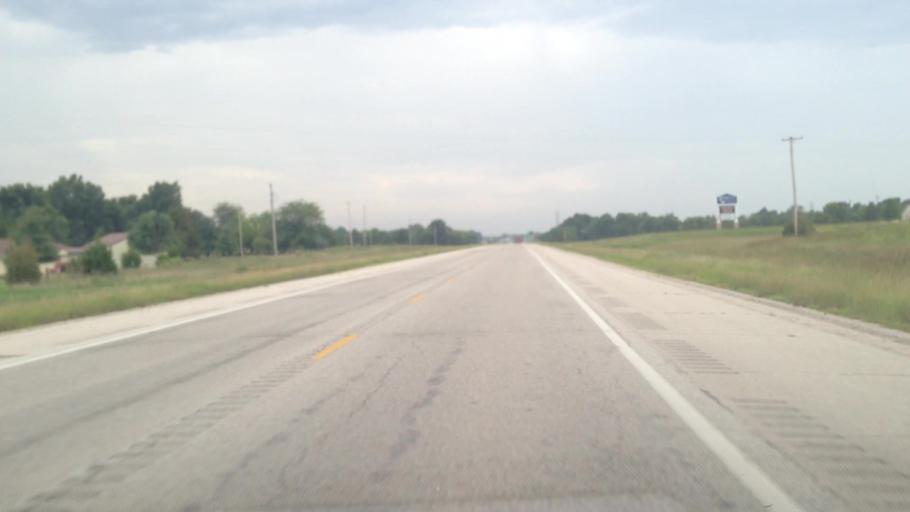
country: US
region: Kansas
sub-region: Cherokee County
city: Baxter Springs
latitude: 37.0828
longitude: -94.7076
